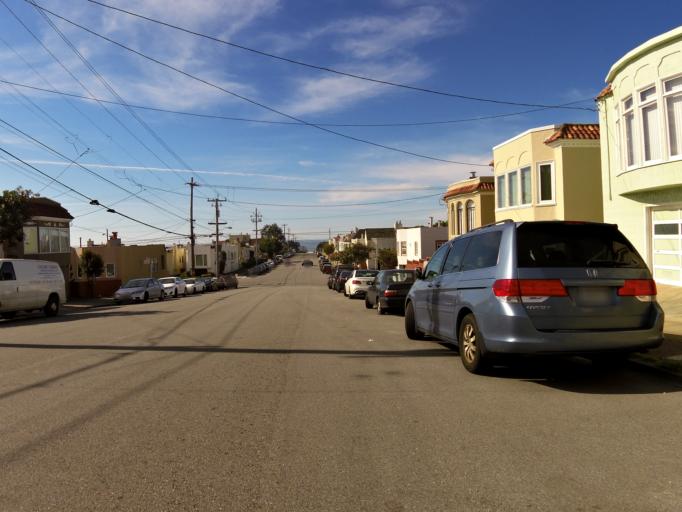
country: US
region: California
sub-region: San Mateo County
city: Daly City
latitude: 37.7445
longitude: -122.4878
